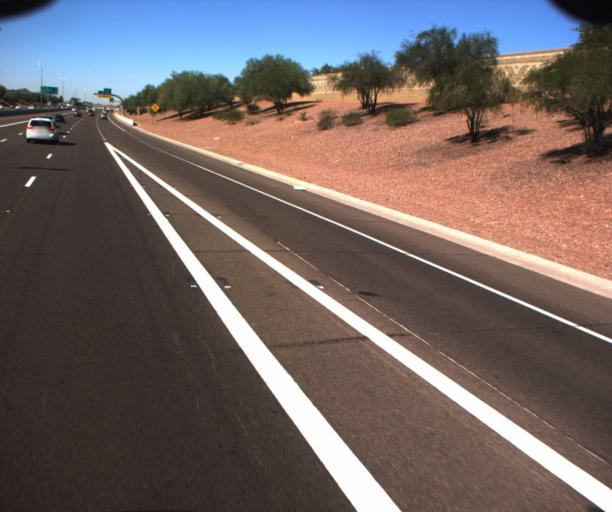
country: US
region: Arizona
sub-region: Maricopa County
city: Peoria
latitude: 33.6679
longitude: -112.2091
